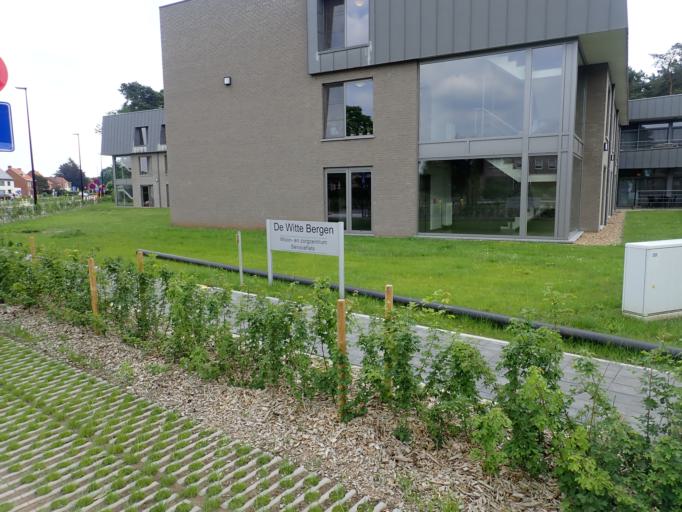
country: BE
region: Flanders
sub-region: Provincie Antwerpen
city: Kasterlee
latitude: 51.2244
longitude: 4.9025
